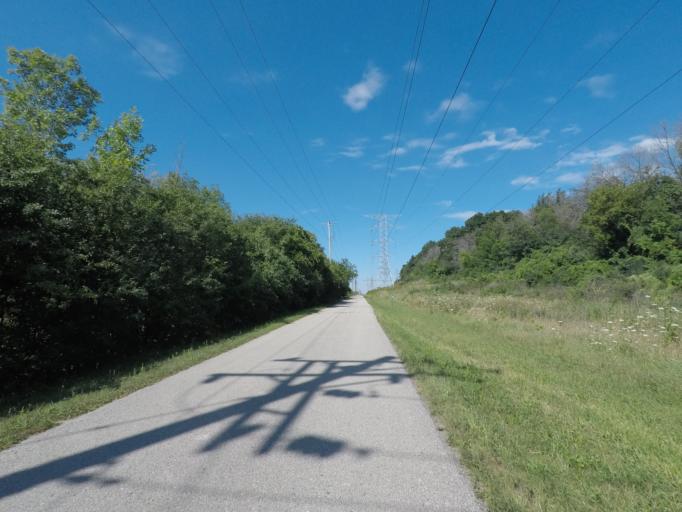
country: US
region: Wisconsin
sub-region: Waukesha County
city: Waukesha
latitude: 43.0100
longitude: -88.1679
